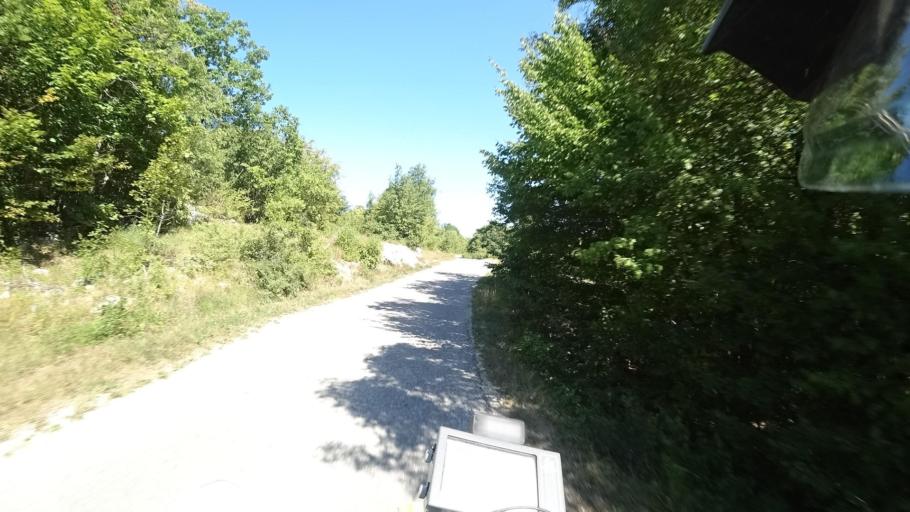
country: HR
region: Licko-Senjska
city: Otocac
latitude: 44.7322
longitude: 15.3353
